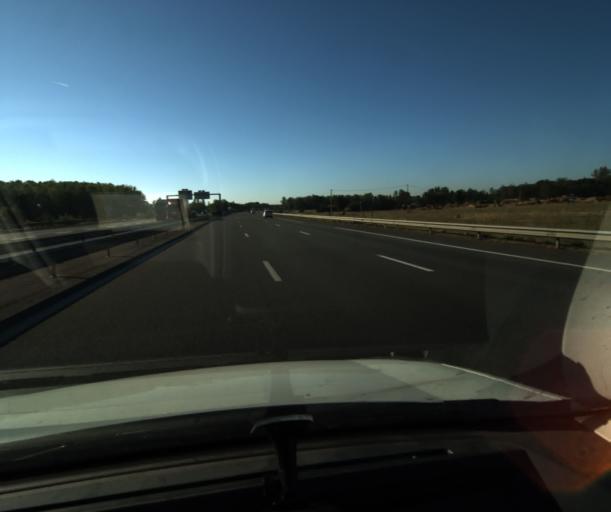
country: FR
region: Midi-Pyrenees
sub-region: Departement du Tarn-et-Garonne
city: Campsas
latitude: 43.9249
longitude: 1.3126
